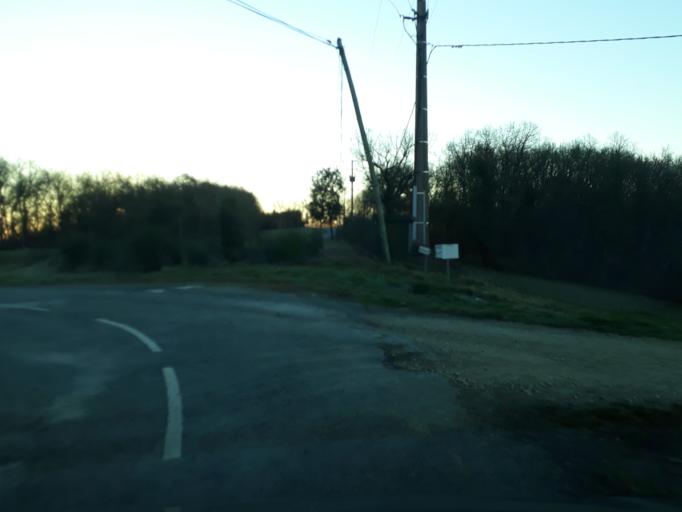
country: FR
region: Midi-Pyrenees
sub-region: Departement du Gers
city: Pavie
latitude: 43.6085
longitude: 0.6836
